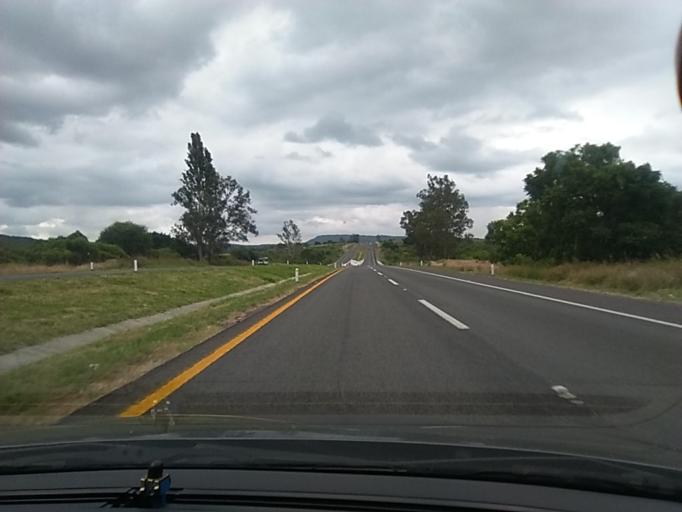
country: MX
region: Jalisco
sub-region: Zapotlanejo
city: La Mezquitera
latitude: 20.5524
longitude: -103.0489
